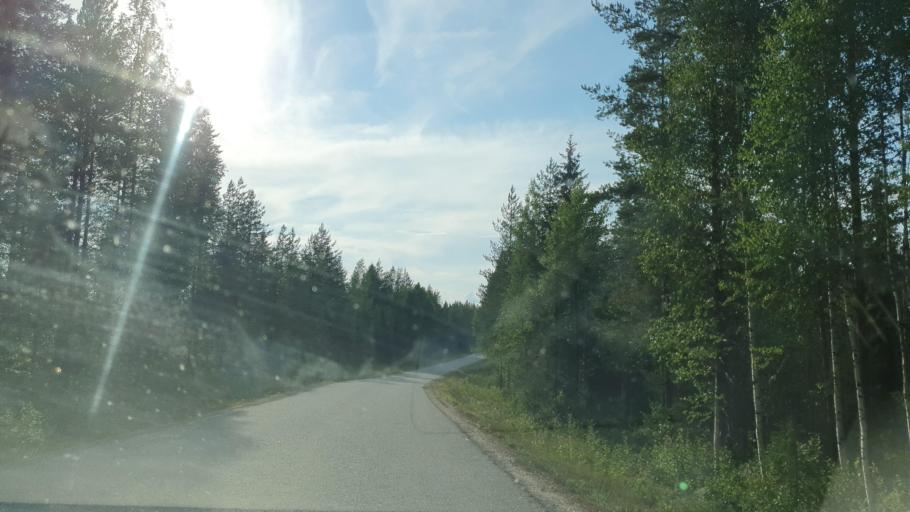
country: FI
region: Kainuu
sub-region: Kehys-Kainuu
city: Kuhmo
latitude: 64.2769
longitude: 29.4336
